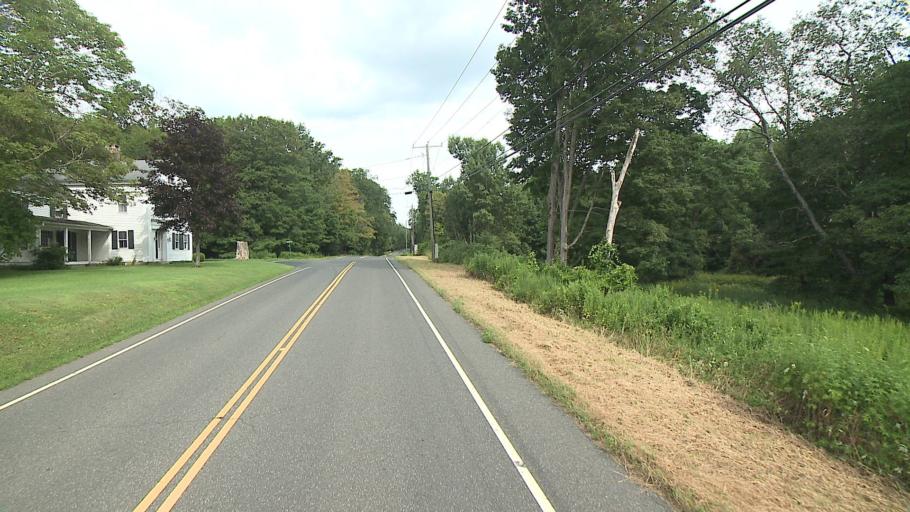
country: US
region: Connecticut
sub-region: Litchfield County
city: Woodbury
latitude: 41.5844
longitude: -73.2505
